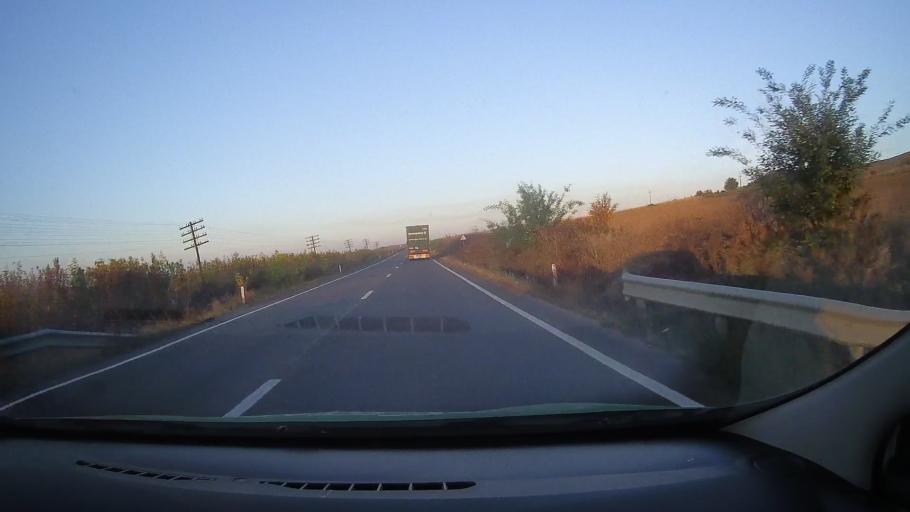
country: RO
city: Dioszeg
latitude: 47.3047
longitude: 22.0230
